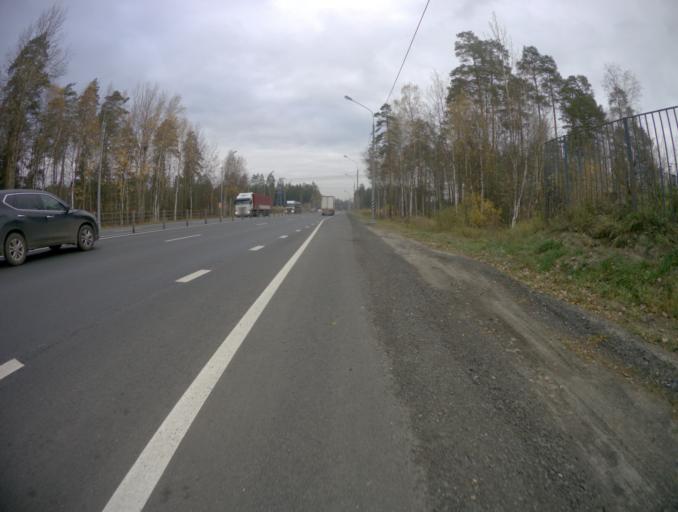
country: RU
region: Moskovskaya
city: Malaya Dubna
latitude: 55.8515
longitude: 38.9636
